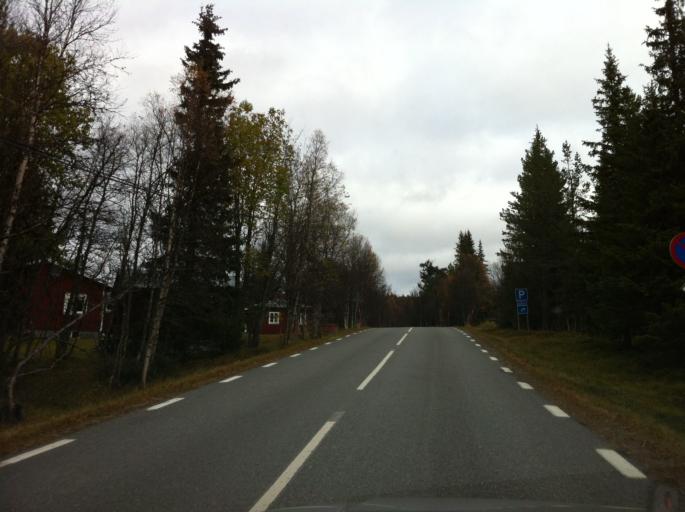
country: NO
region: Hedmark
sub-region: Engerdal
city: Engerdal
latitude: 62.0922
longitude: 12.3070
